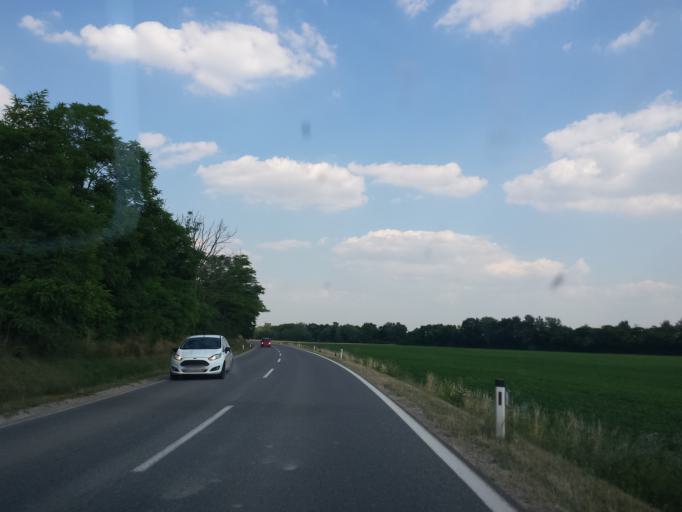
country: AT
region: Lower Austria
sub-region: Politischer Bezirk Ganserndorf
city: Parbasdorf
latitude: 48.2792
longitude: 16.5990
